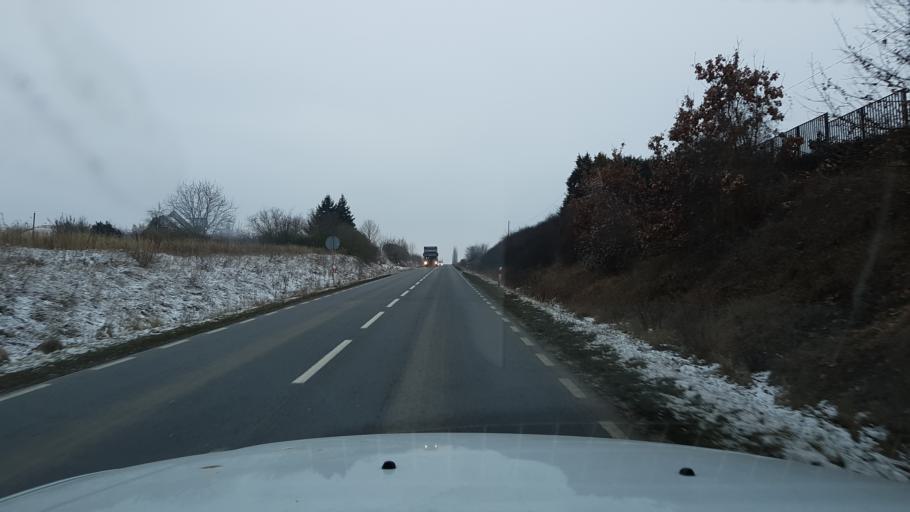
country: PL
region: West Pomeranian Voivodeship
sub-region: Powiat gryfinski
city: Chojna
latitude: 52.9568
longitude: 14.4159
